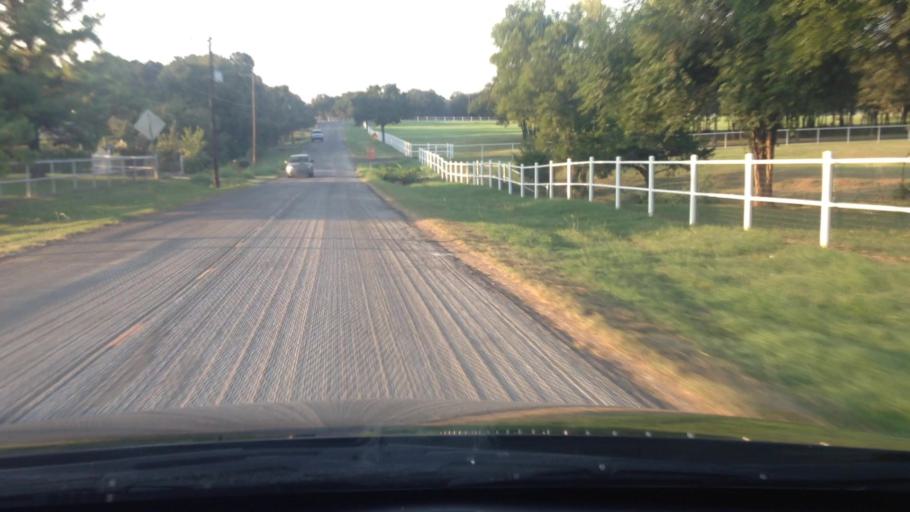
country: US
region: Texas
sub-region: Tarrant County
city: Rendon
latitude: 32.5986
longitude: -97.2405
